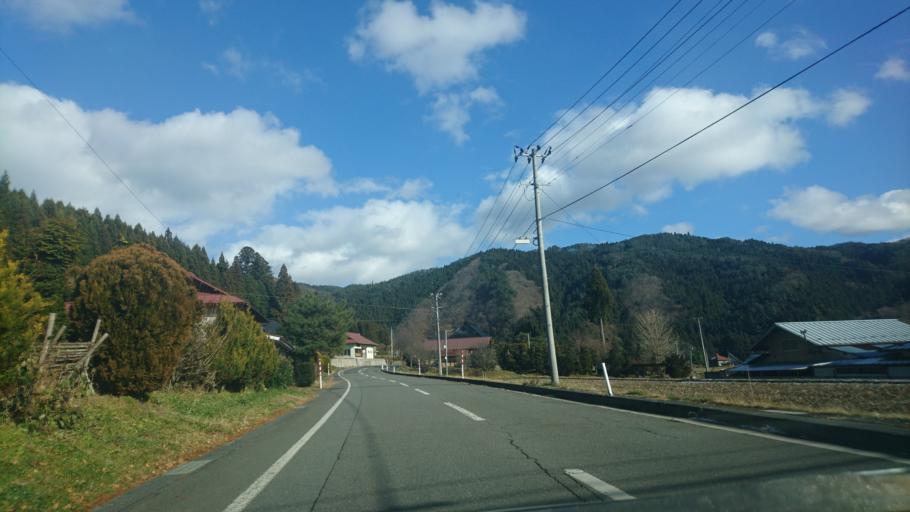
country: JP
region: Iwate
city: Mizusawa
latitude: 39.0742
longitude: 141.3835
